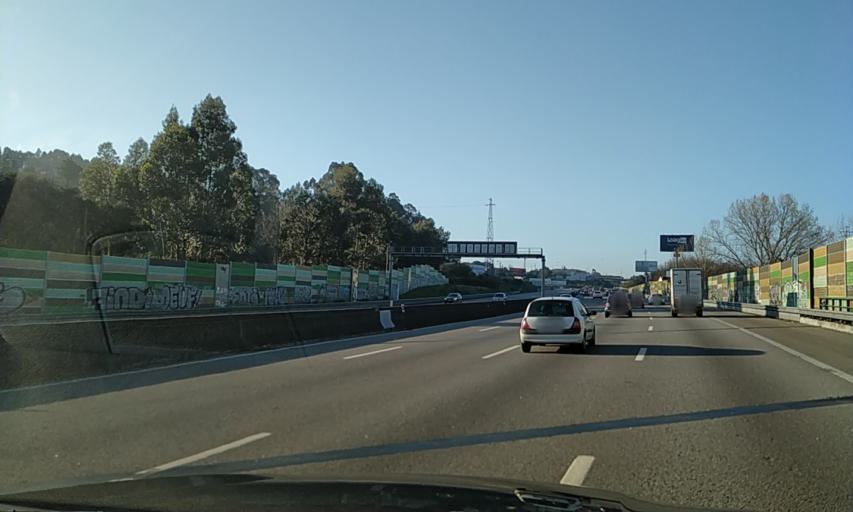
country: PT
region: Porto
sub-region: Maia
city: Aguas Santas
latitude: 41.2073
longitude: -8.5827
